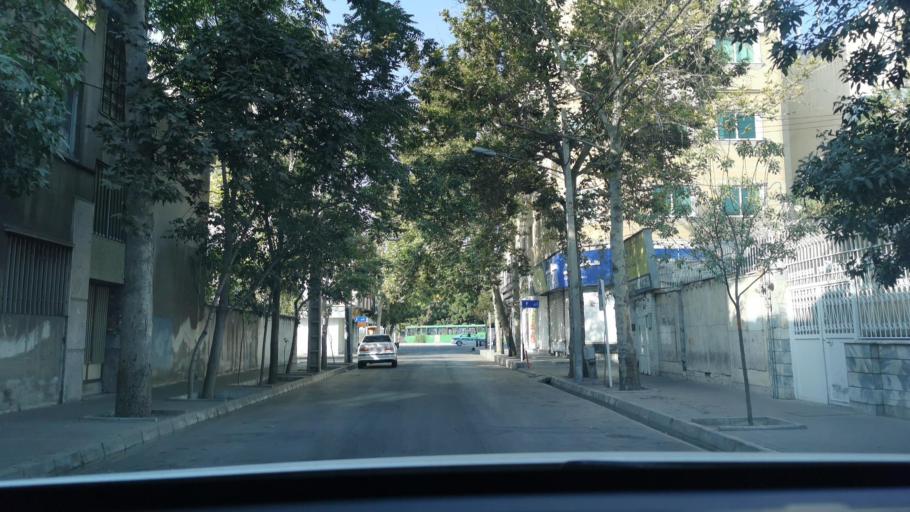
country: IR
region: Razavi Khorasan
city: Mashhad
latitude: 36.2936
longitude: 59.5832
